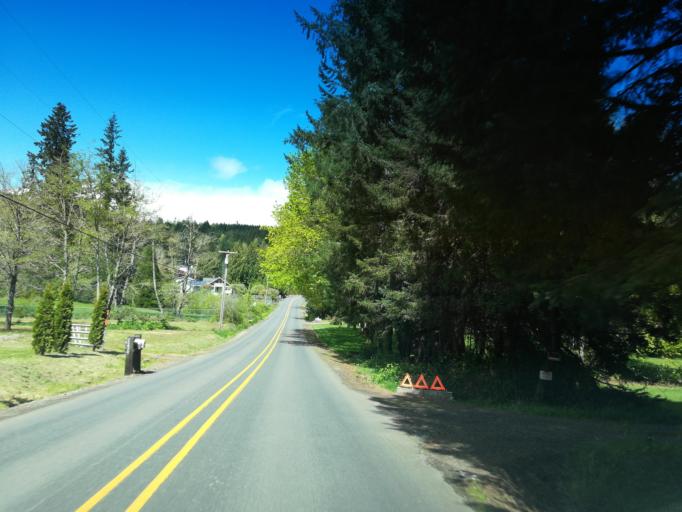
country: US
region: Oregon
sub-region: Clackamas County
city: Damascus
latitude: 45.4485
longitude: -122.4211
